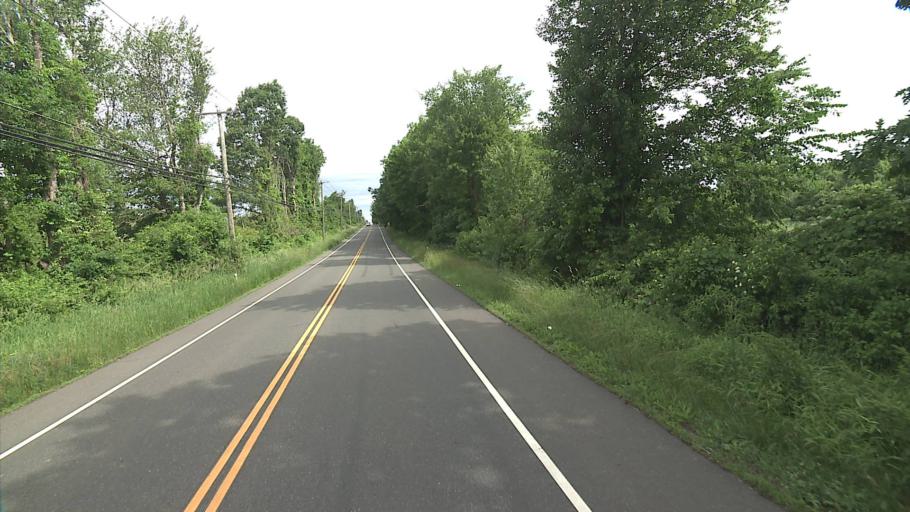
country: US
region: Connecticut
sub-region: Litchfield County
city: Watertown
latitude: 41.6339
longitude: -73.1403
